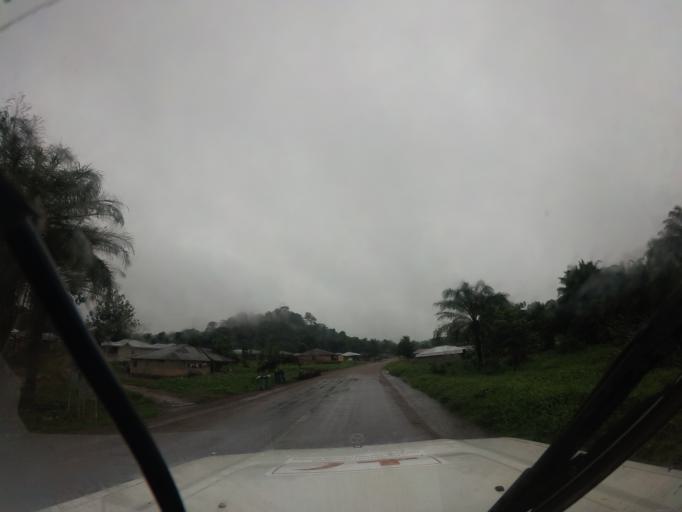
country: SL
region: Northern Province
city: Kabala
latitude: 9.4673
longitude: -11.6766
